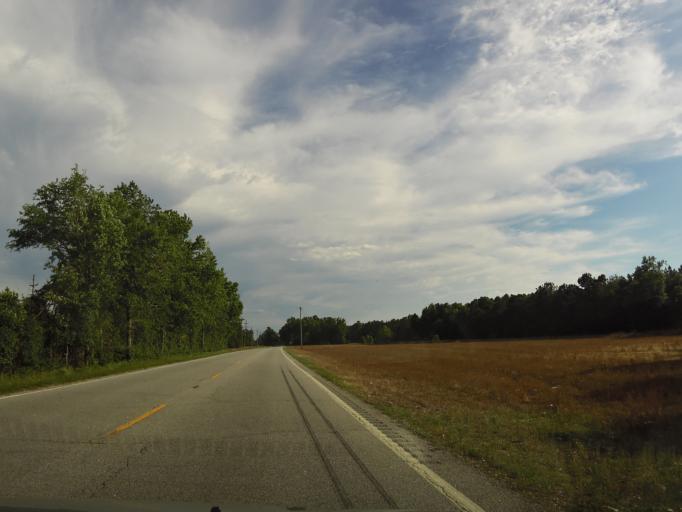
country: US
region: South Carolina
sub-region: Hampton County
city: Estill
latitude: 32.8539
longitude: -81.2382
